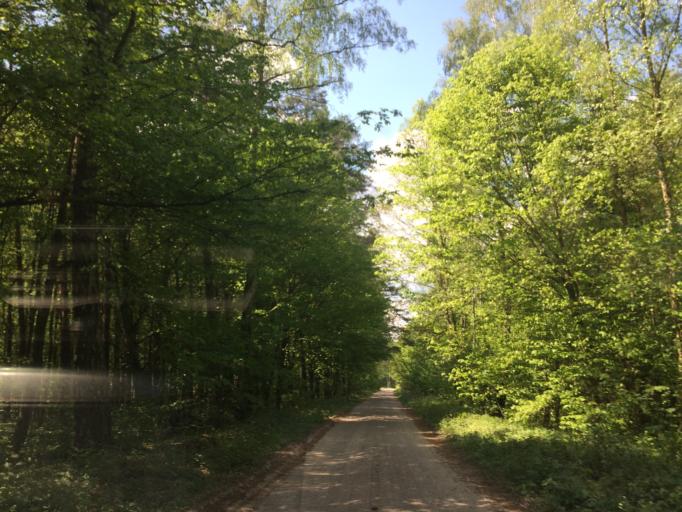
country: PL
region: Warmian-Masurian Voivodeship
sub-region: Powiat nowomiejski
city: Nowe Miasto Lubawskie
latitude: 53.4497
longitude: 19.6281
